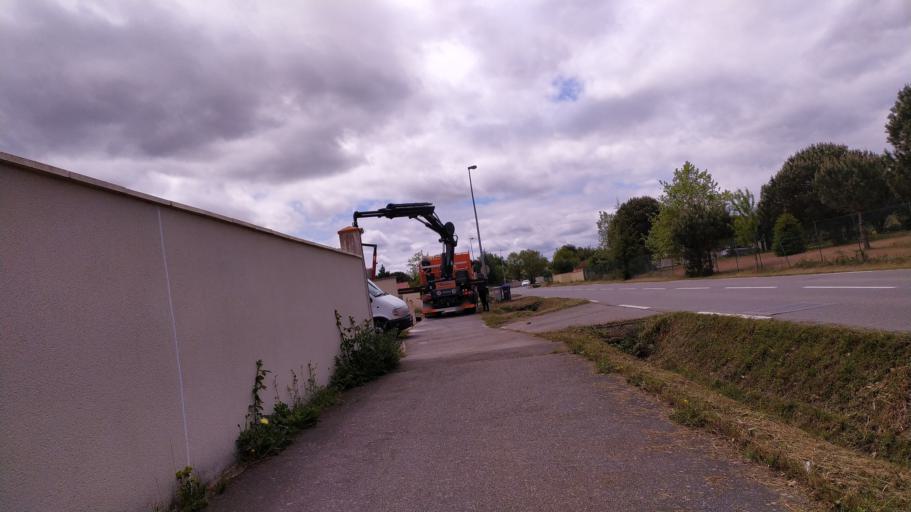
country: FR
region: Midi-Pyrenees
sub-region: Departement de la Haute-Garonne
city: Tournefeuille
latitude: 43.5825
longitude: 1.3052
